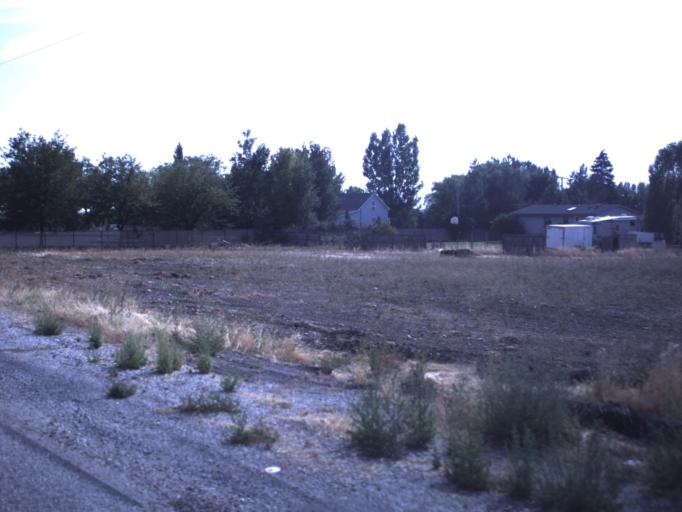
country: US
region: Utah
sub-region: Box Elder County
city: Honeyville
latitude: 41.6387
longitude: -112.0796
